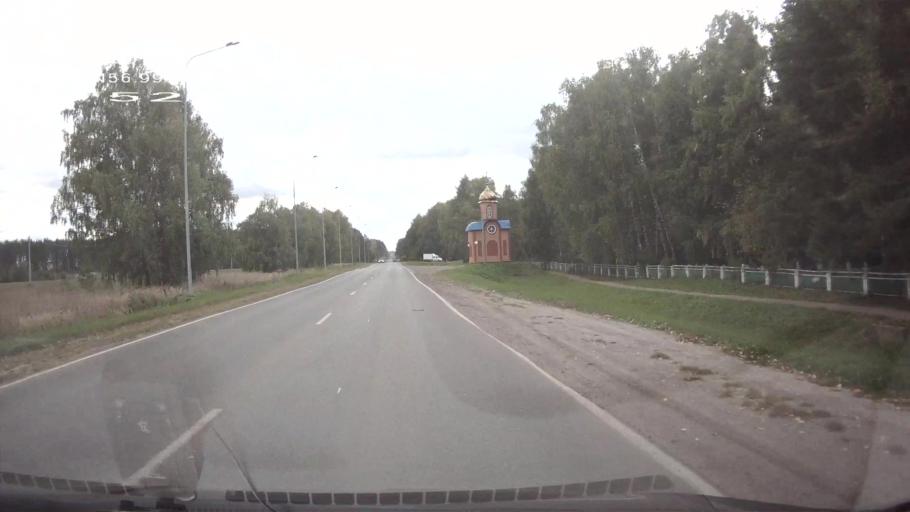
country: RU
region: Mariy-El
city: Kuzhener
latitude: 56.9939
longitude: 48.7427
